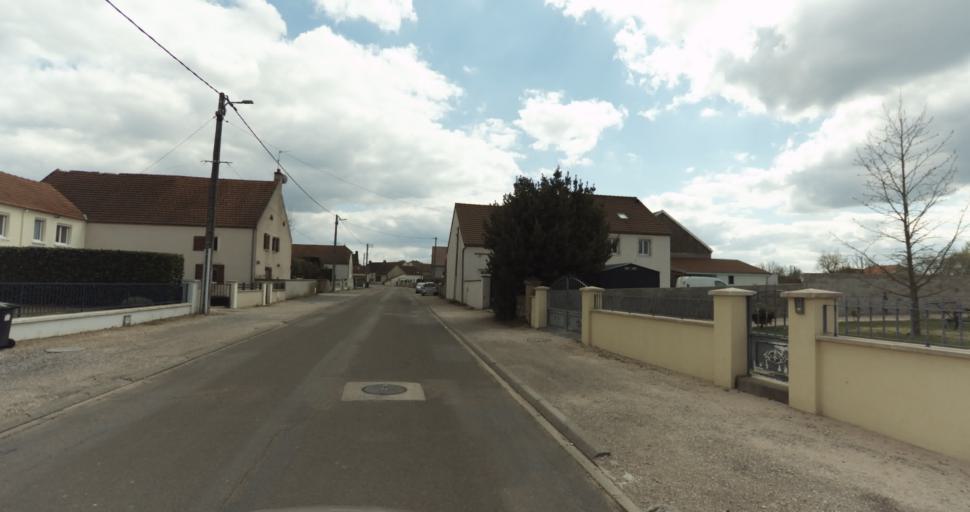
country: FR
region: Bourgogne
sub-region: Departement de la Cote-d'Or
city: Auxonne
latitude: 47.1871
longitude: 5.3911
